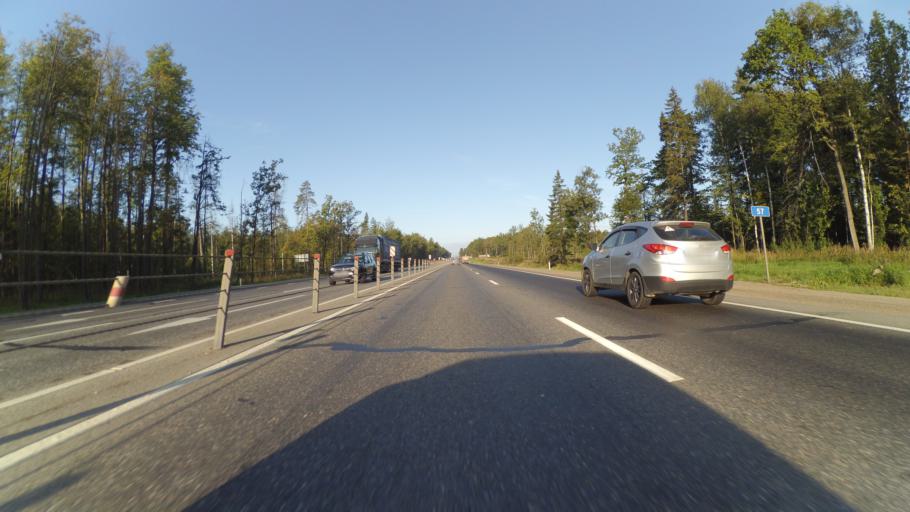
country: RU
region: Moskovskaya
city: Kubinka
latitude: 55.5824
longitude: 36.8060
